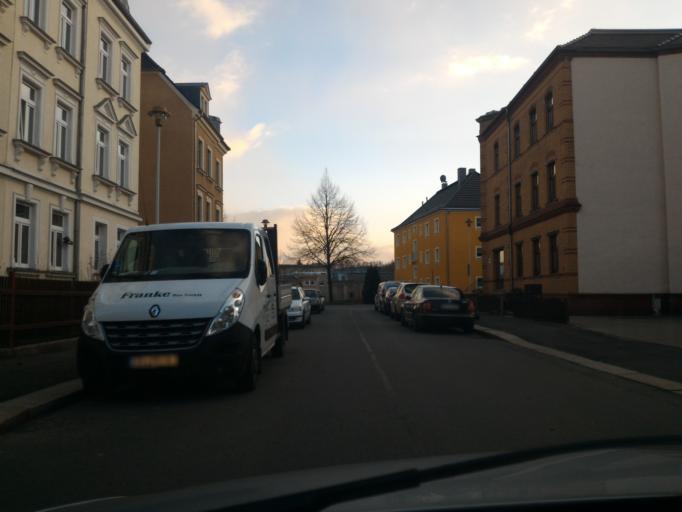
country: DE
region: Saxony
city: Zittau
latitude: 50.8949
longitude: 14.7909
